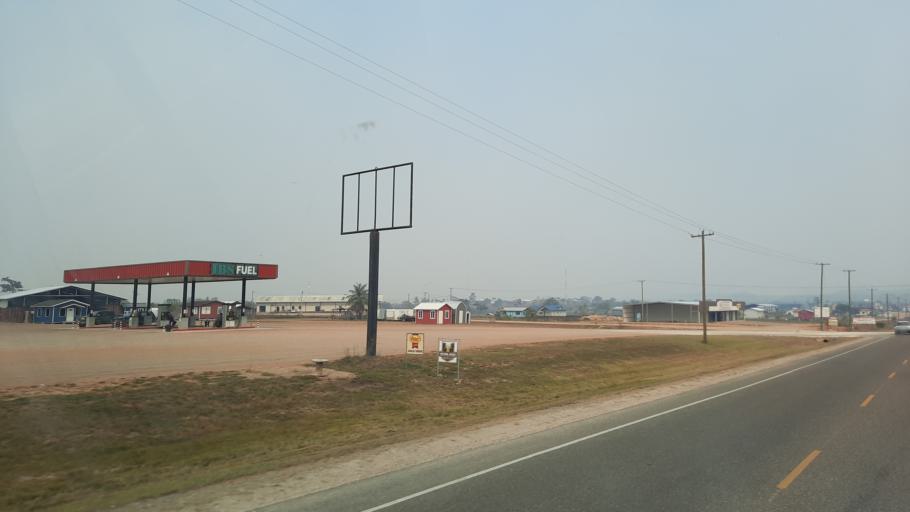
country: BZ
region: Cayo
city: Valley of Peace
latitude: 17.2395
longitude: -88.9441
